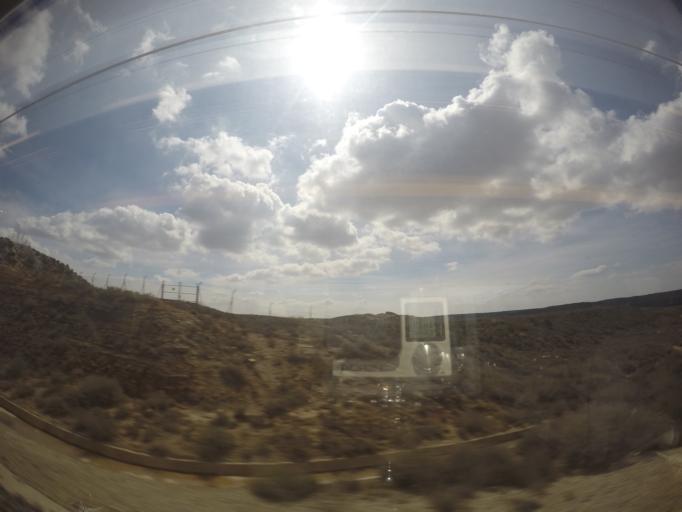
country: ES
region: Aragon
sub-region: Provincia de Huesca
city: Candasnos
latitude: 41.5246
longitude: 0.0151
